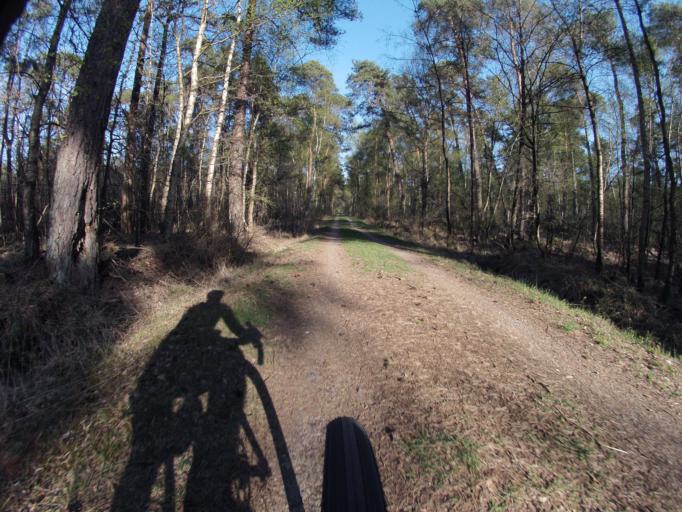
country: DE
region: Lower Saxony
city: Schuttorf
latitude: 52.3618
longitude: 7.2350
